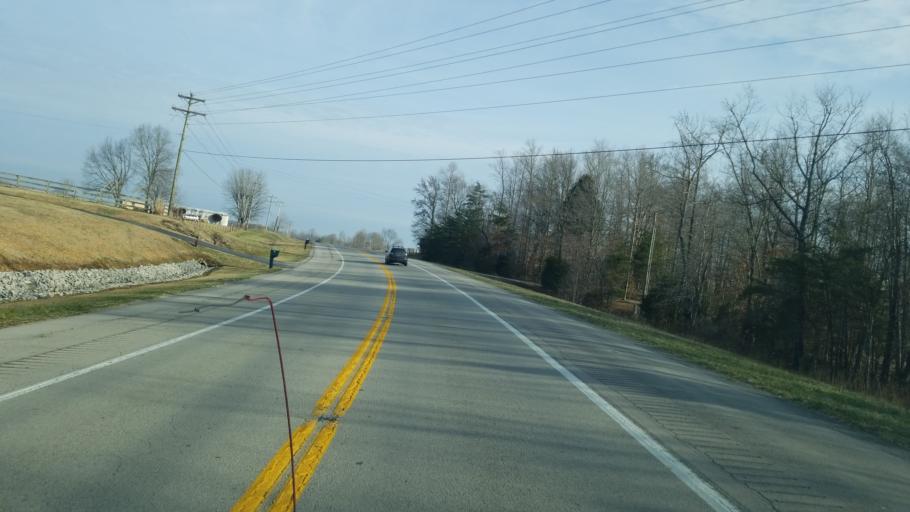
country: US
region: Kentucky
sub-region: Russell County
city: Russell Springs
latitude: 37.1123
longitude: -85.0507
